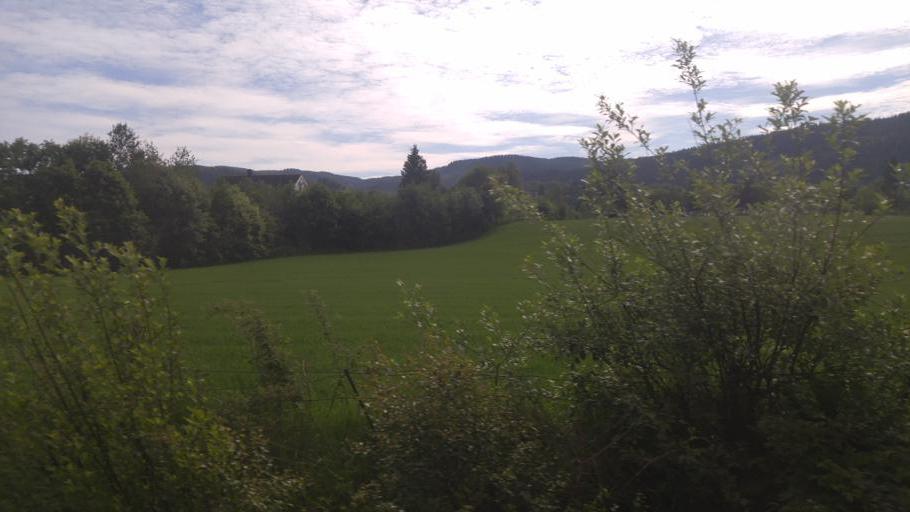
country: NO
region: Sor-Trondelag
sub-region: Melhus
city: Lundamo
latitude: 63.1797
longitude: 10.3077
